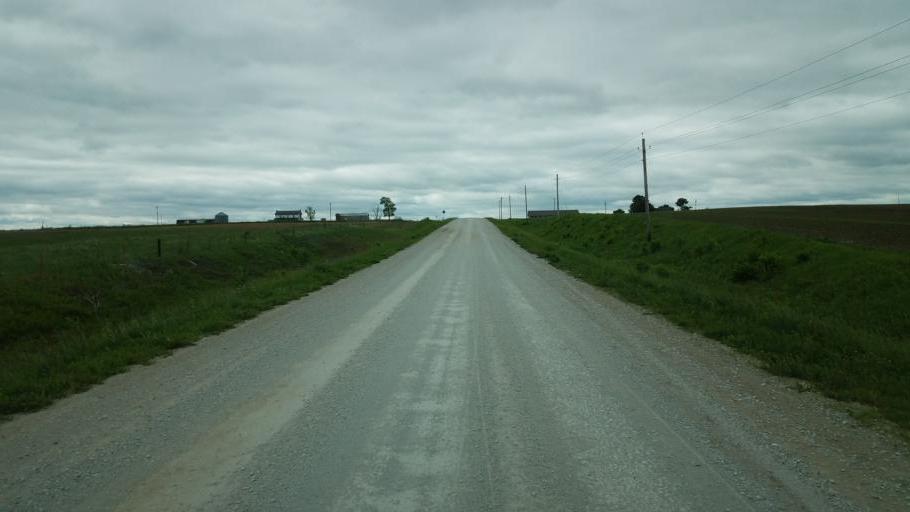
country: US
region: Iowa
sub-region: Decatur County
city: Lamoni
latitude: 40.6411
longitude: -93.9200
